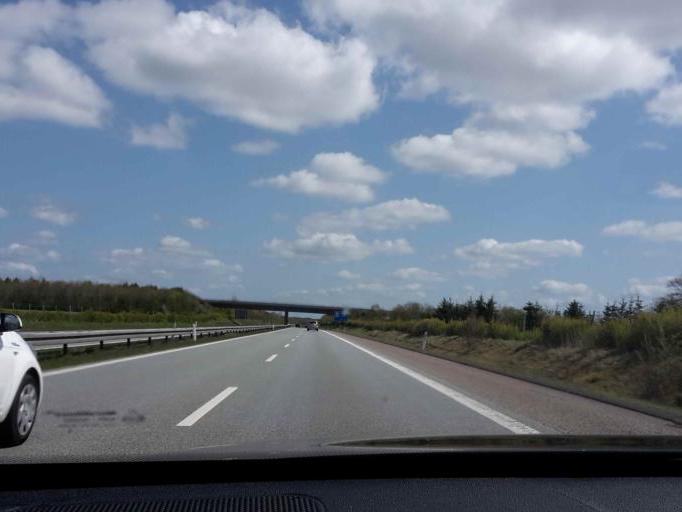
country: DK
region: South Denmark
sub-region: Vejen Kommune
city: Vejen
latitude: 55.4949
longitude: 9.1089
